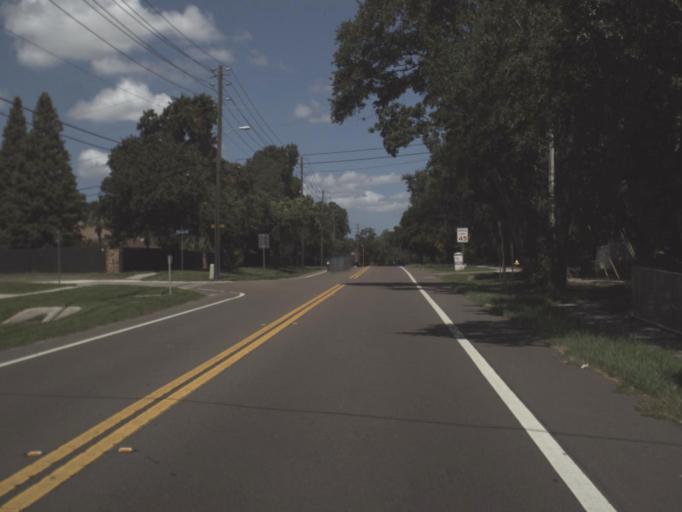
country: US
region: Florida
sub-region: Pinellas County
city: Safety Harbor
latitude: 28.0155
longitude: -82.6851
